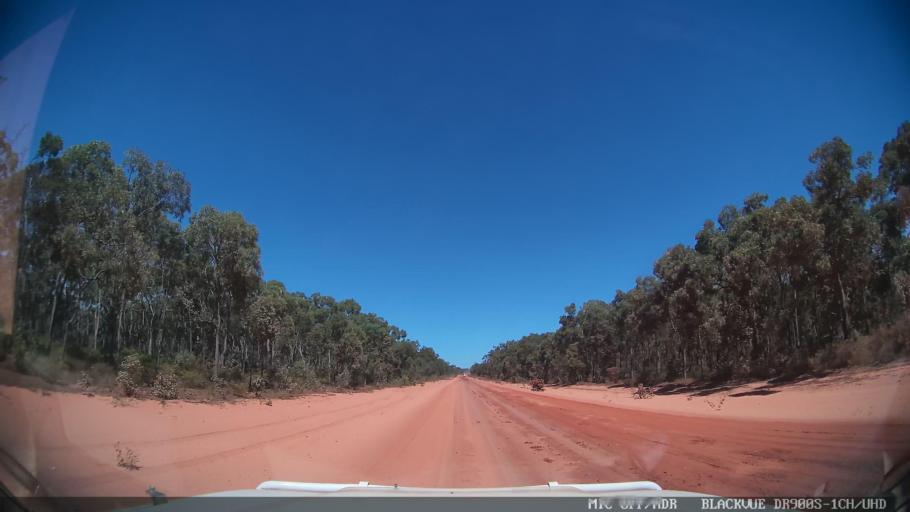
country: AU
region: Queensland
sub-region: Torres
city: Thursday Island
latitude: -11.3688
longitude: 142.3479
